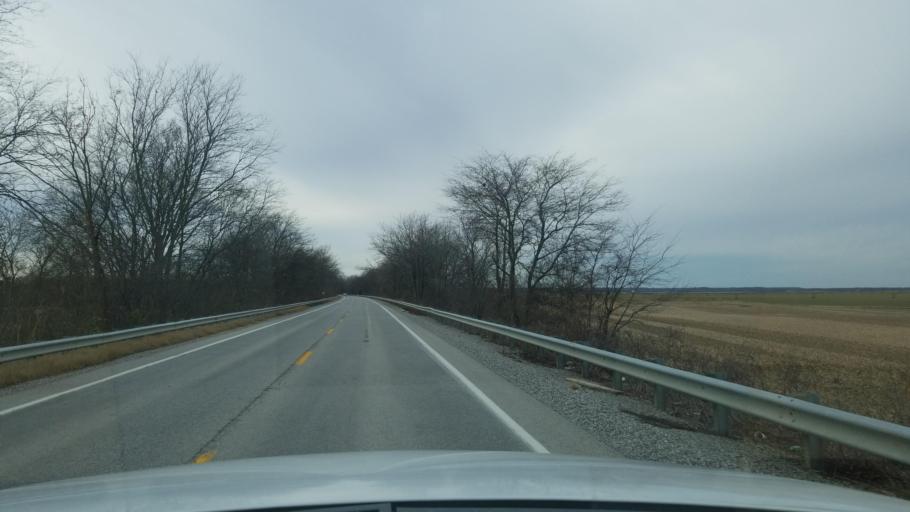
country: US
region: Indiana
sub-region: Posey County
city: Mount Vernon
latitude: 37.9427
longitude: -88.0555
